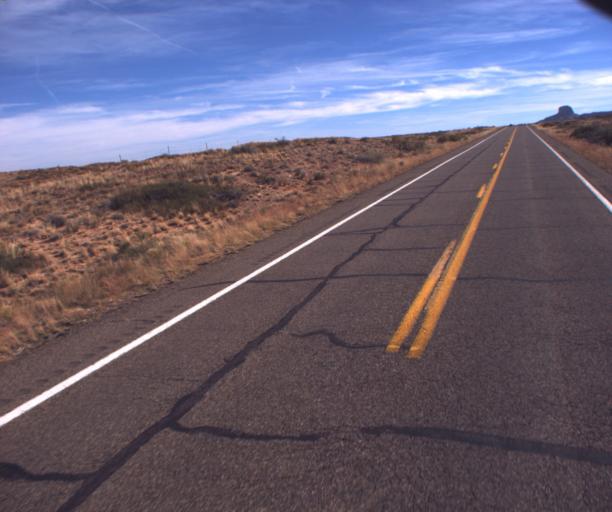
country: US
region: Arizona
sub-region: Coconino County
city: Kaibito
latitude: 36.6121
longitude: -111.0202
